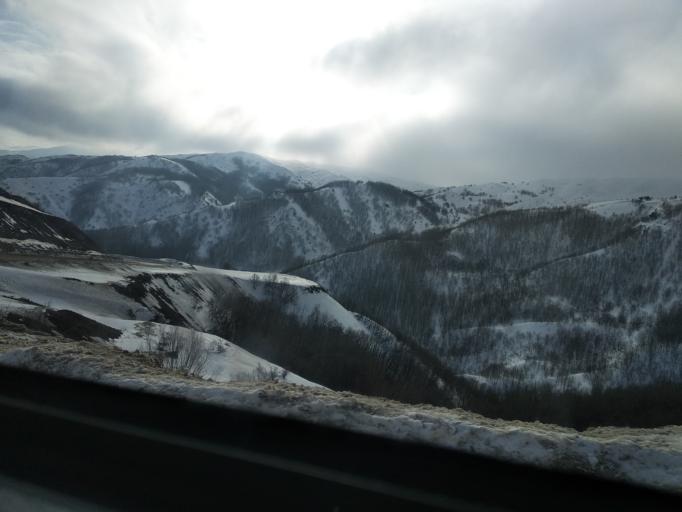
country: TR
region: Erzincan
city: Catalarmut
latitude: 39.8970
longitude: 39.3851
